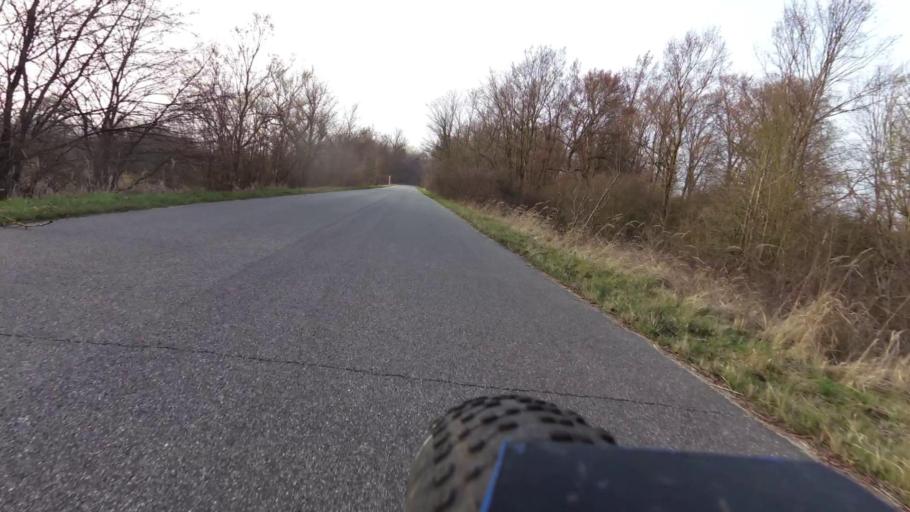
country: DE
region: Brandenburg
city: Vogelsang
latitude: 52.2486
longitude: 14.7057
